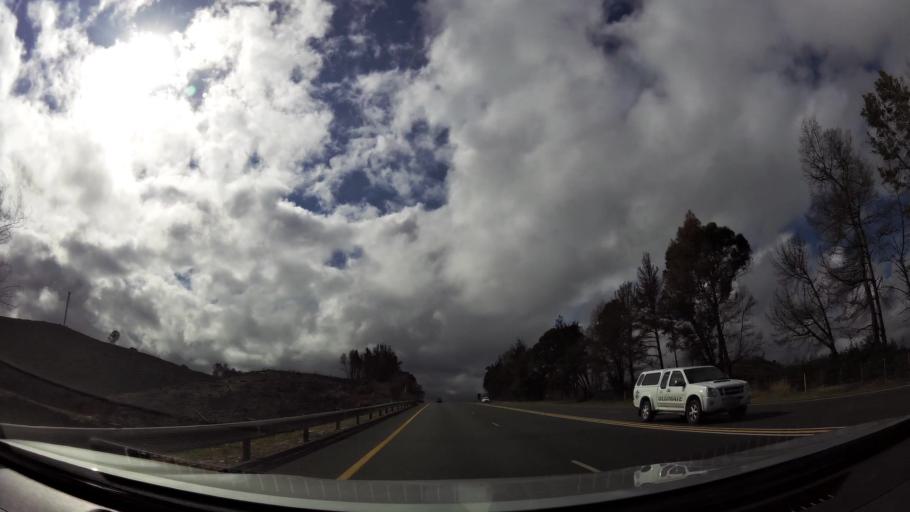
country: ZA
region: Western Cape
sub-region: Eden District Municipality
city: Knysna
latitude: -34.0382
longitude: 23.1214
